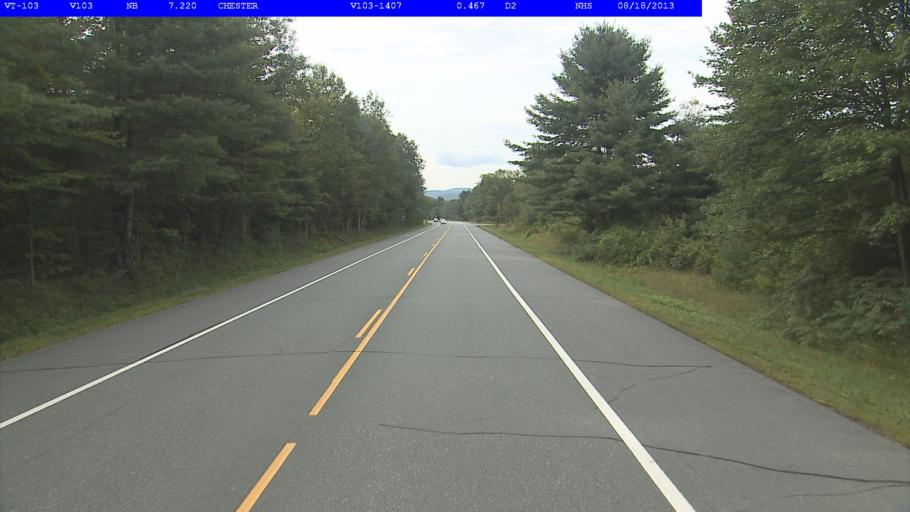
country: US
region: Vermont
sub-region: Windsor County
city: Chester
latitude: 43.2395
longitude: -72.5601
